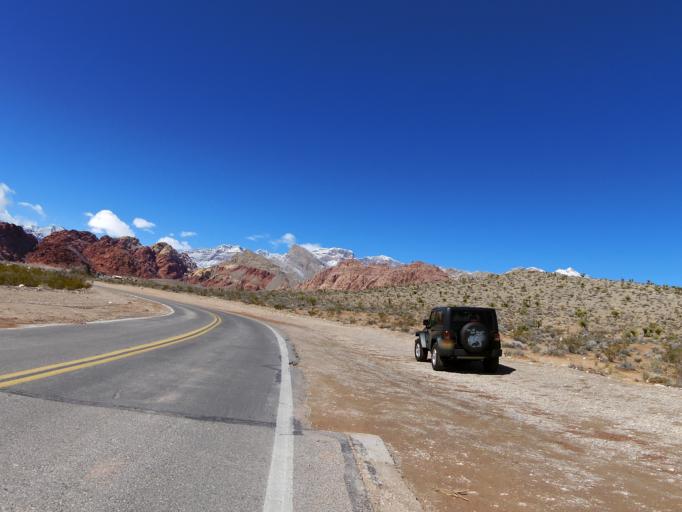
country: US
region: Nevada
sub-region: Clark County
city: Summerlin South
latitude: 36.1460
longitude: -115.4048
